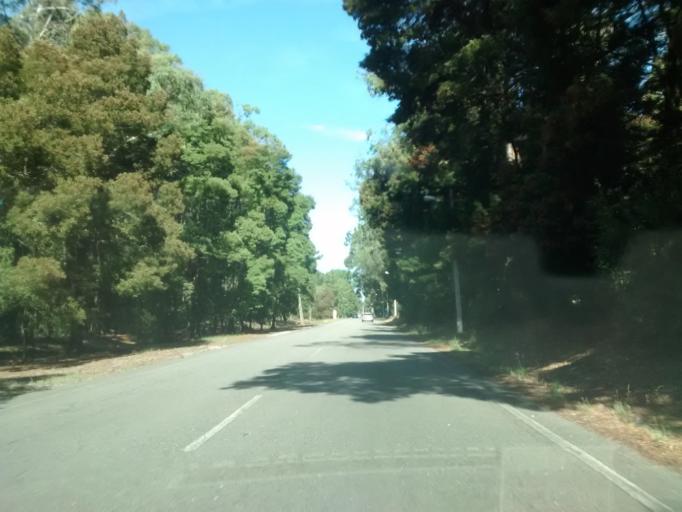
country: PT
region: Coimbra
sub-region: Mira
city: Mira
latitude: 40.4508
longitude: -8.7705
